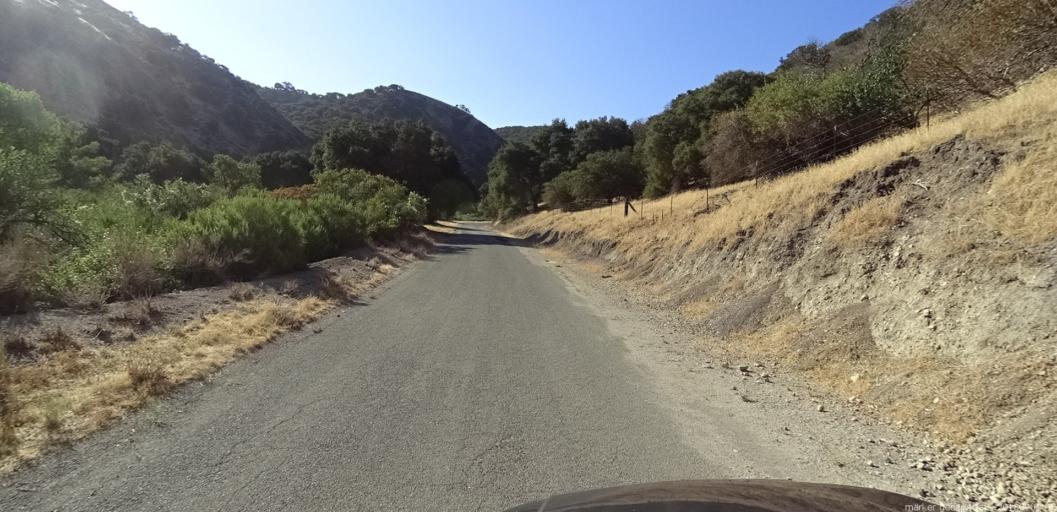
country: US
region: California
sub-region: Monterey County
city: Greenfield
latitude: 36.2208
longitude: -121.2789
